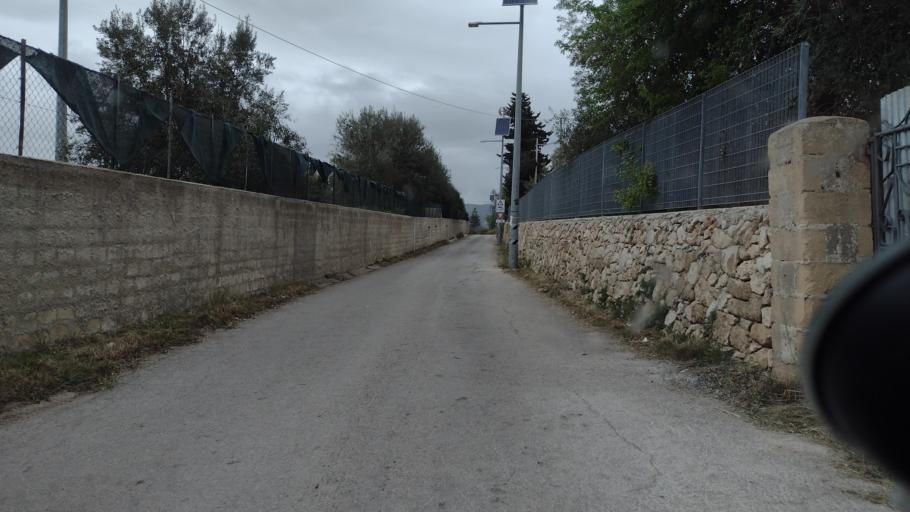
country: IT
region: Sicily
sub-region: Provincia di Siracusa
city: Avola
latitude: 36.8950
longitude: 15.1153
